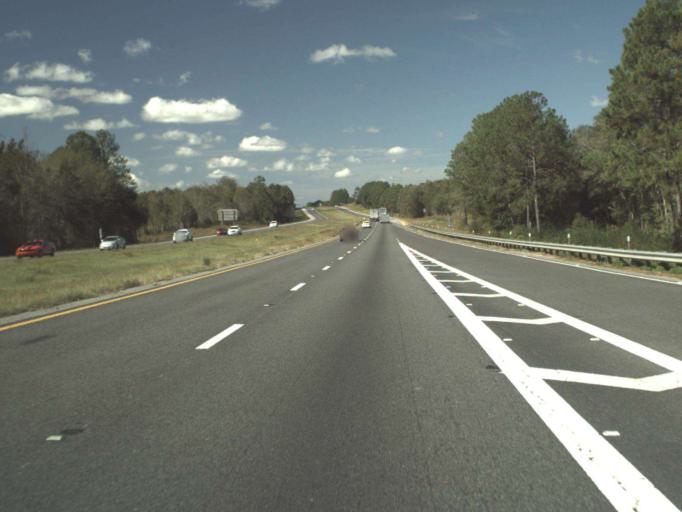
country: US
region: Florida
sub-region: Washington County
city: Chipley
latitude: 30.7491
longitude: -85.5570
